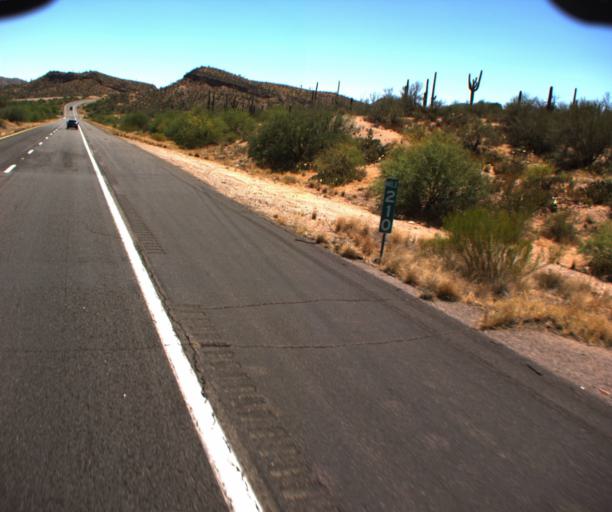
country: US
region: Arizona
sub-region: Maricopa County
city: Rio Verde
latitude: 33.7597
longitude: -111.4966
